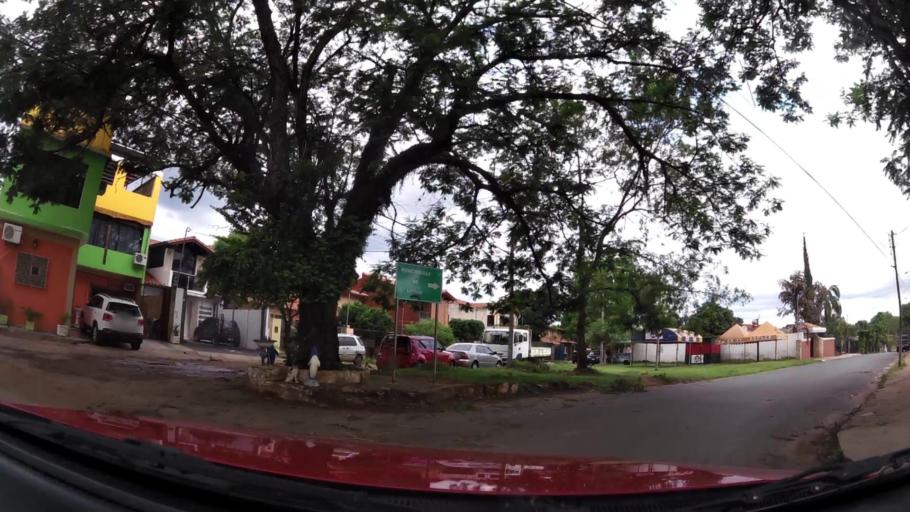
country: PY
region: Central
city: San Lorenzo
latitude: -25.2786
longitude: -57.4912
